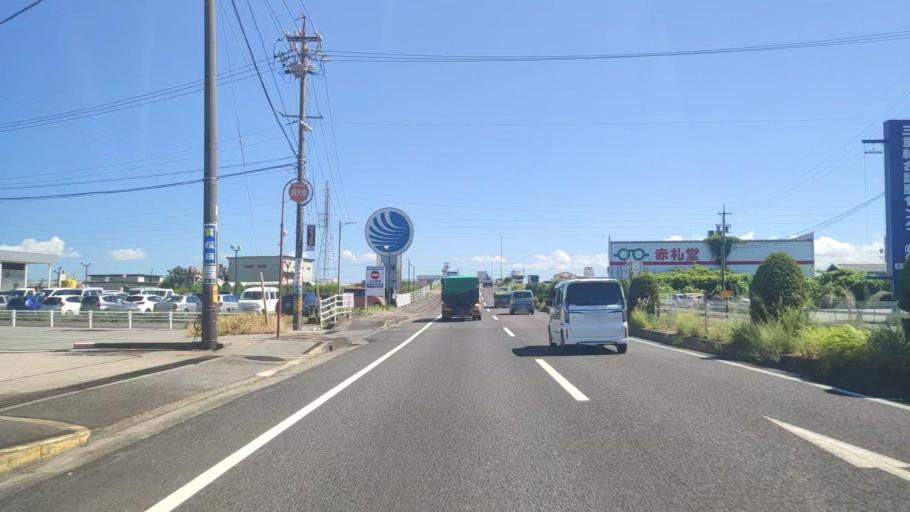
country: JP
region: Mie
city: Tsu-shi
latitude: 34.6811
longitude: 136.5181
